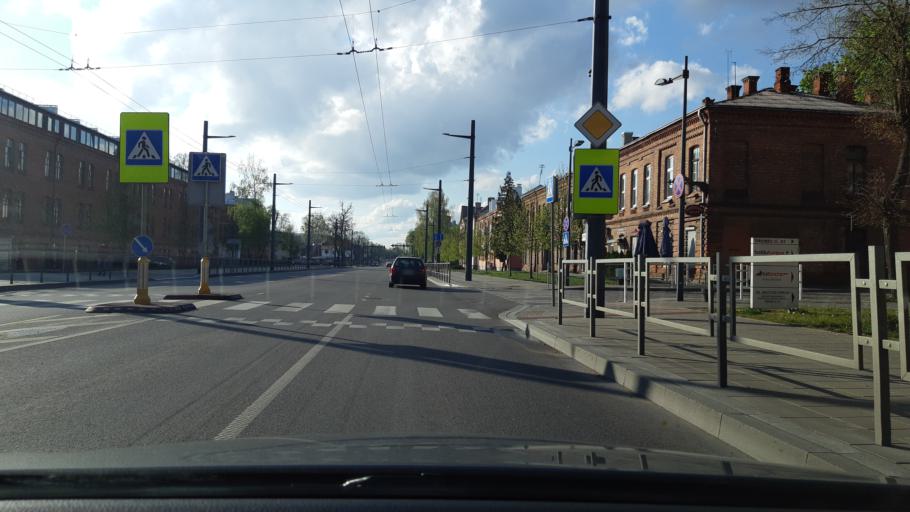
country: LT
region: Kauno apskritis
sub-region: Kaunas
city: Aleksotas
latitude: 54.8692
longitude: 23.9421
